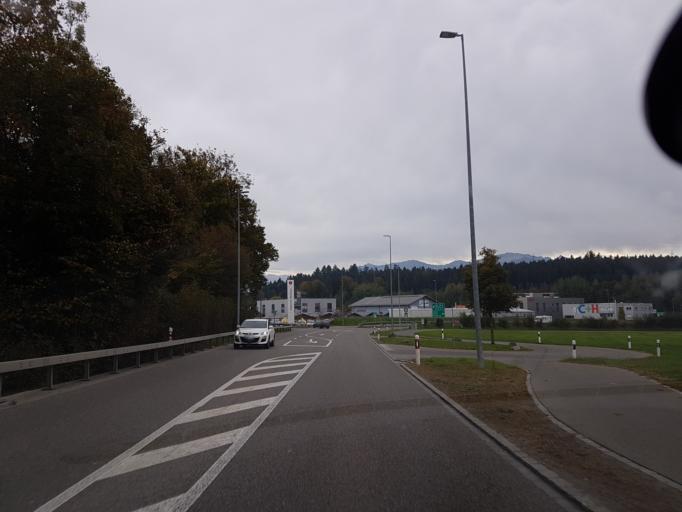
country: CH
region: Saint Gallen
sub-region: Wahlkreis See-Gaster
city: Schmerikon
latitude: 47.2398
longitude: 8.9501
